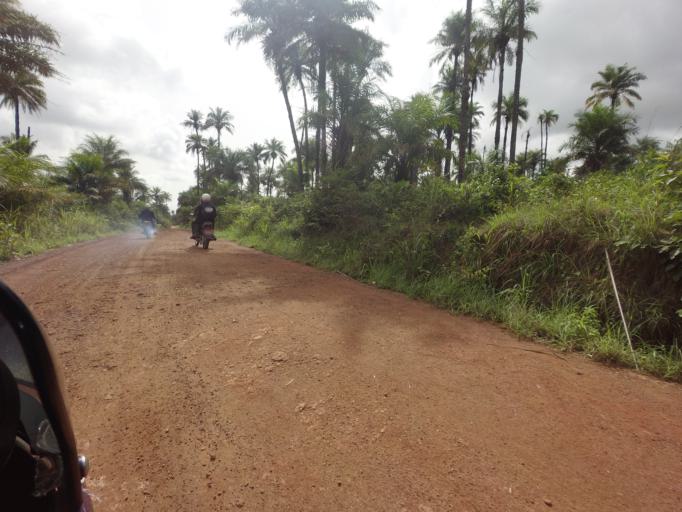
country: SL
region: Northern Province
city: Kambia
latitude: 9.1041
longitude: -12.9614
